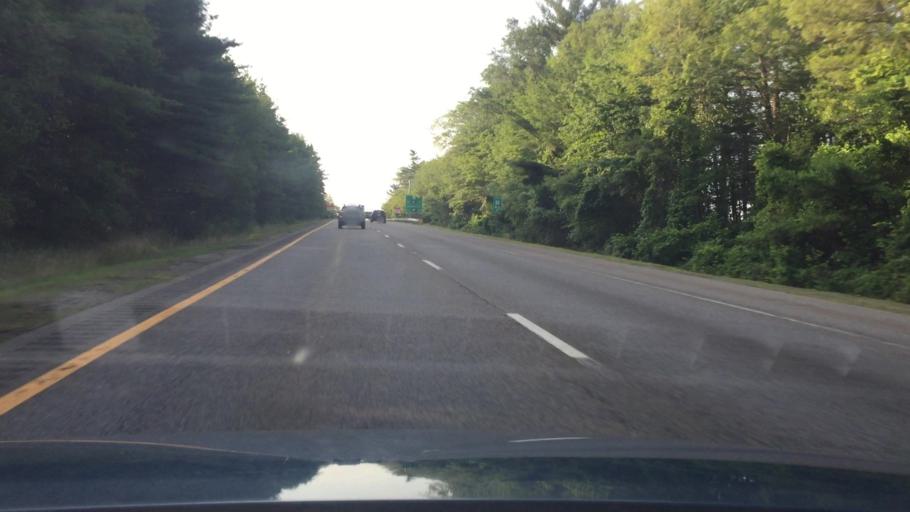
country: US
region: Massachusetts
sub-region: Plymouth County
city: North Pembroke
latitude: 42.1101
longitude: -70.7699
